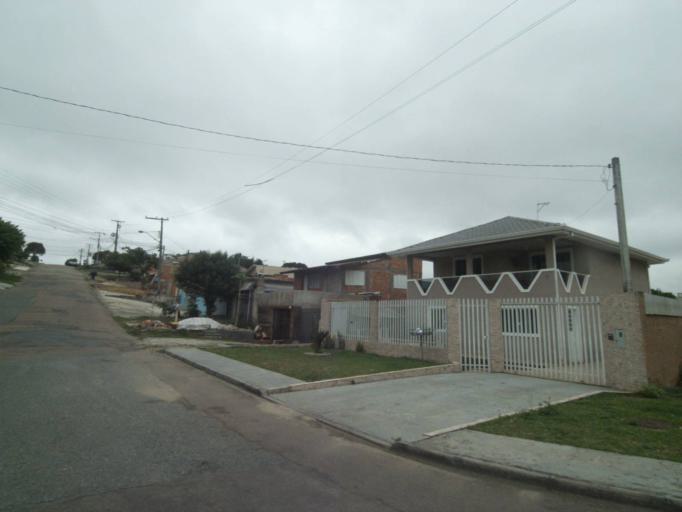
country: BR
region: Parana
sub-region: Sao Jose Dos Pinhais
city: Sao Jose dos Pinhais
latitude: -25.5383
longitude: -49.2860
